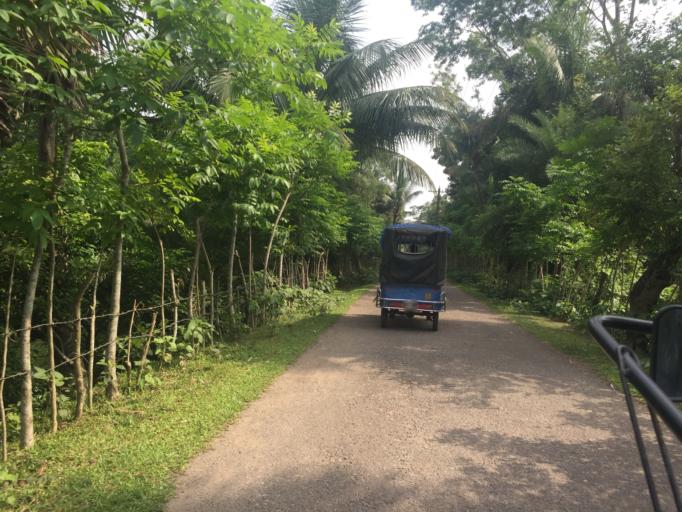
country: BD
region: Barisal
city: Mathba
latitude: 22.2201
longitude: 89.9160
